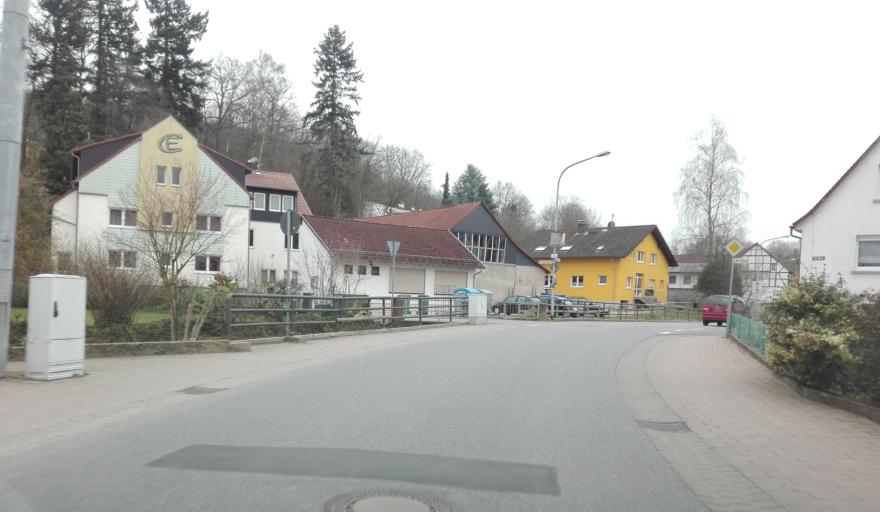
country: DE
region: Hesse
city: Lutzelbach
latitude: 49.7457
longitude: 8.7149
